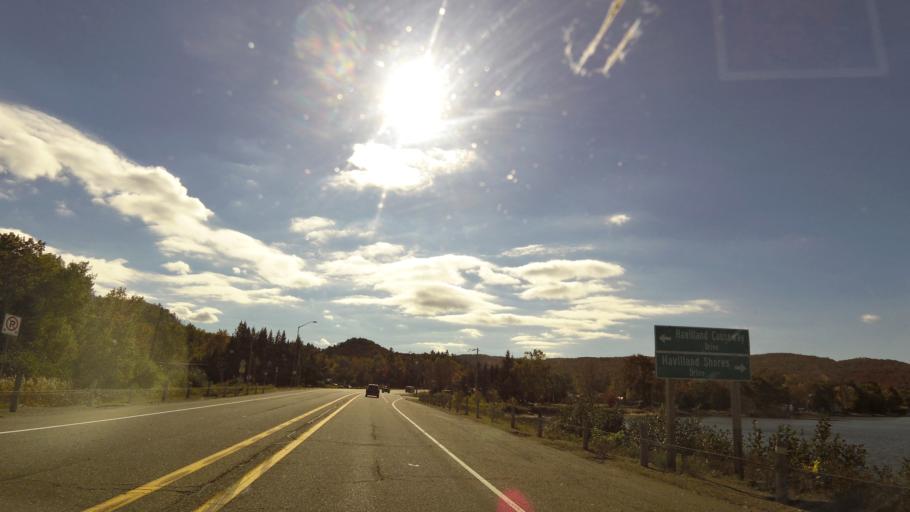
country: CA
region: Ontario
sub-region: Algoma
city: Sault Ste. Marie
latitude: 46.8198
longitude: -84.3990
